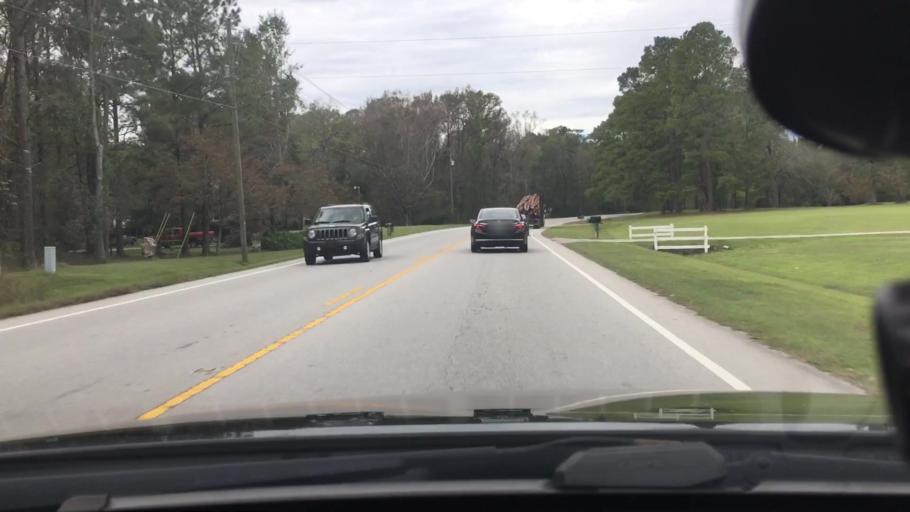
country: US
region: North Carolina
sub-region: Craven County
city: Vanceboro
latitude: 35.2281
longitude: -77.0714
